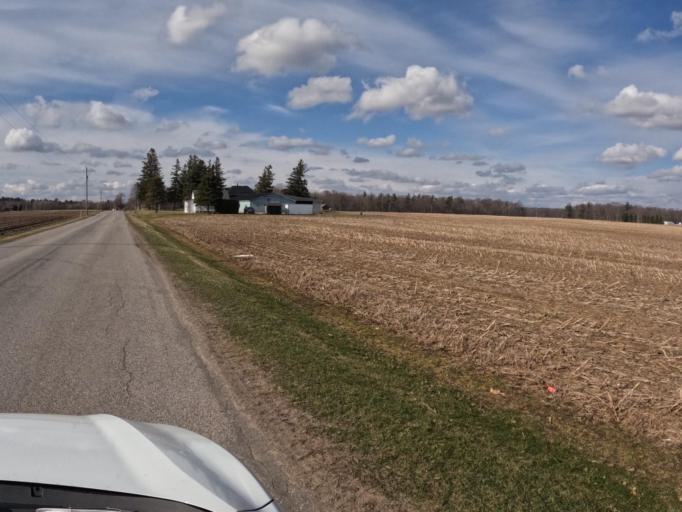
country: CA
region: Ontario
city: Norfolk County
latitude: 42.8824
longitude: -80.2825
